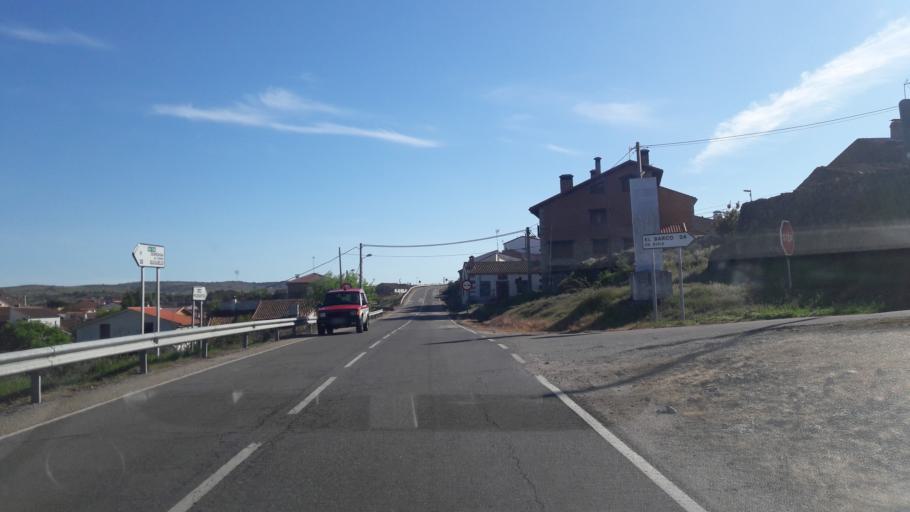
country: ES
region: Castille and Leon
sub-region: Provincia de Avila
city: Narrillos del Alamo
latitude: 40.5347
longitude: -5.4480
